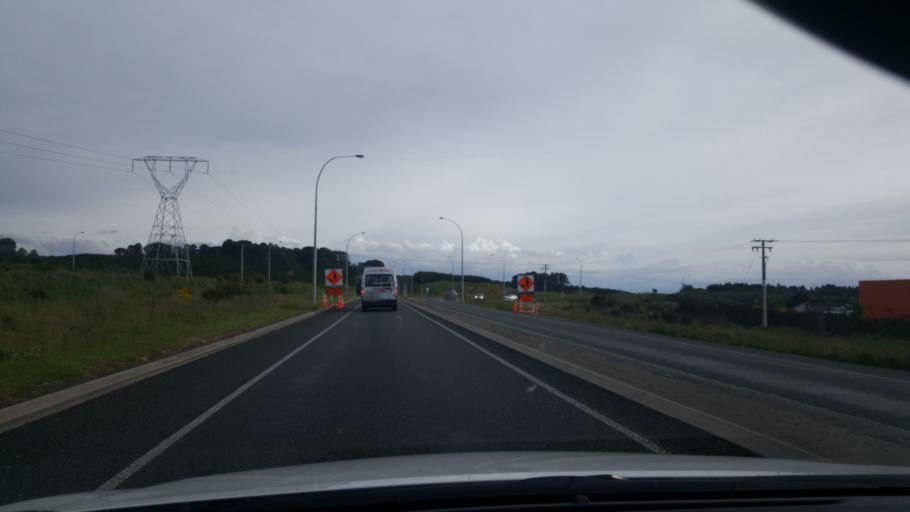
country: NZ
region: Waikato
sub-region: Taupo District
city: Taupo
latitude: -38.7027
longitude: 176.1119
